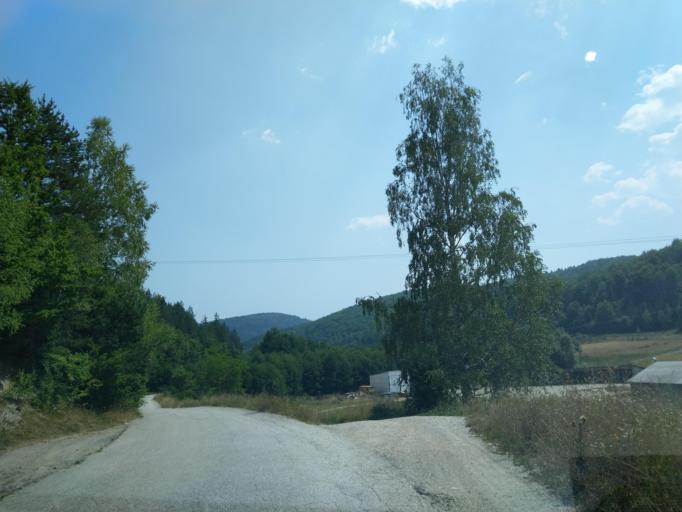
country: RS
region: Central Serbia
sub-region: Zlatiborski Okrug
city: Prijepolje
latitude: 43.3327
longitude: 19.5622
